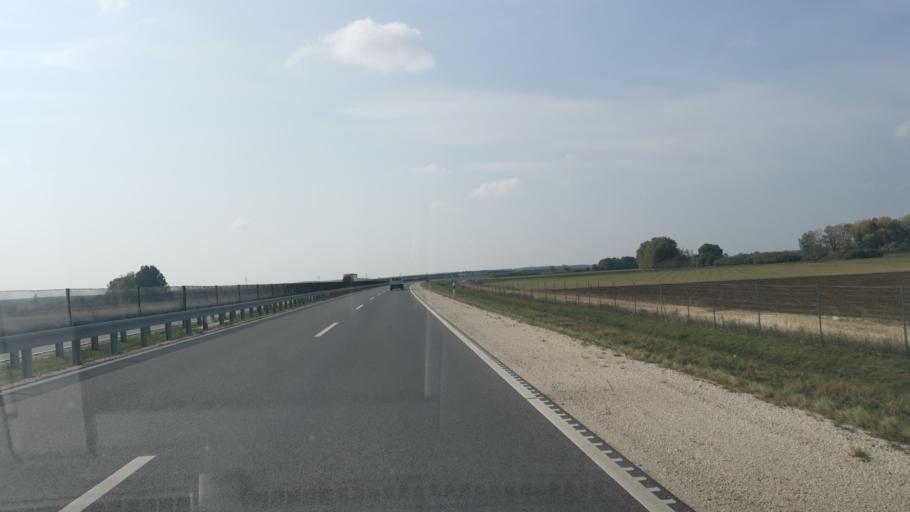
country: HU
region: Gyor-Moson-Sopron
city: Farad
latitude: 47.5734
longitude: 17.1509
